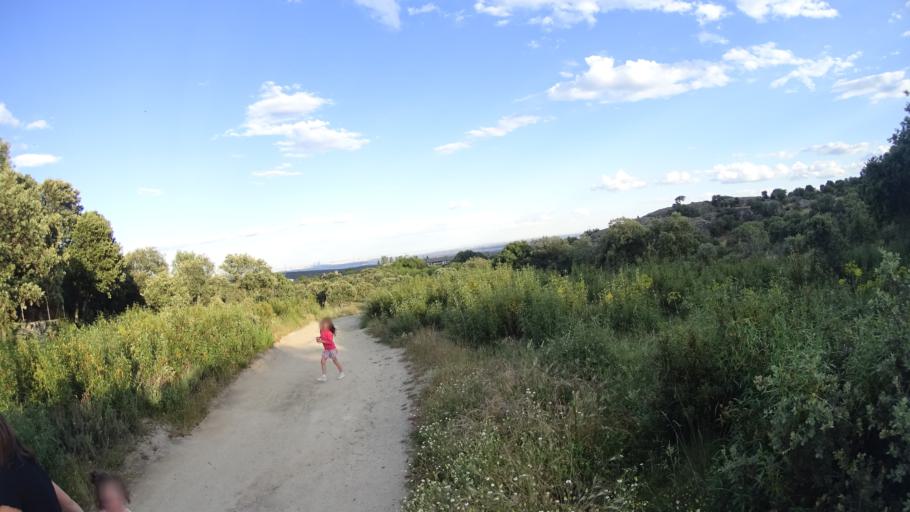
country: ES
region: Madrid
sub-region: Provincia de Madrid
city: Hoyo de Manzanares
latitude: 40.6269
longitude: -3.9163
